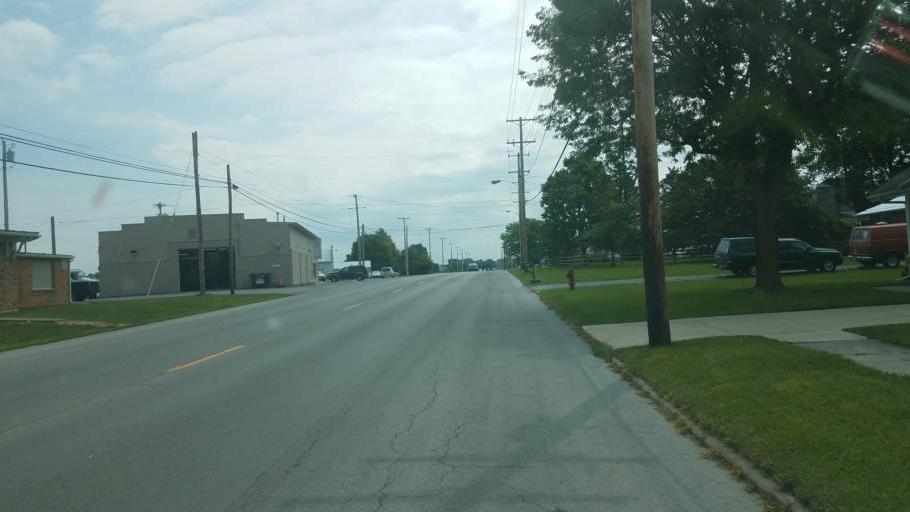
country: US
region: Ohio
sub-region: Wyandot County
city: Carey
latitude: 40.9501
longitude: -83.3687
